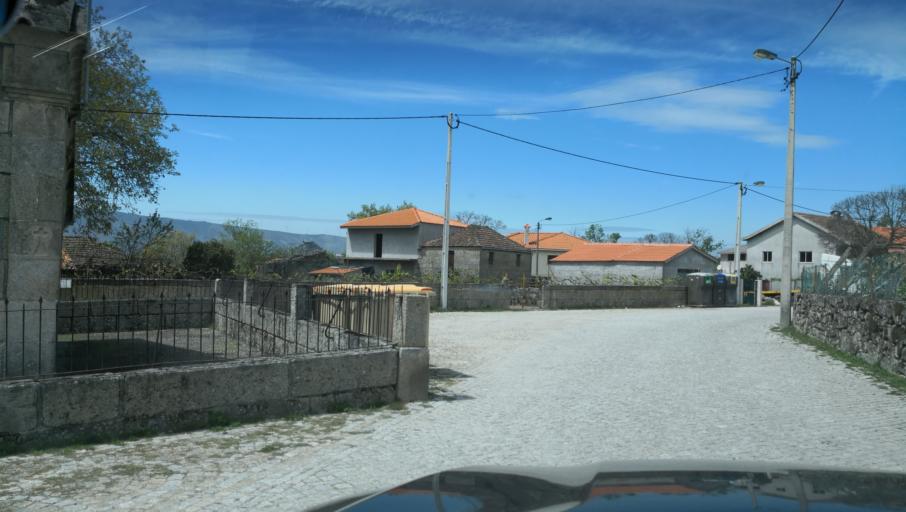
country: PT
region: Vila Real
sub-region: Vila Real
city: Vila Real
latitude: 41.3600
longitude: -7.6667
